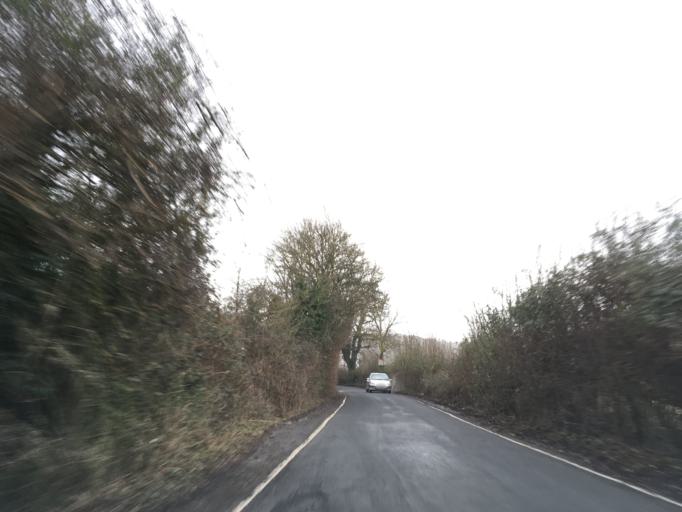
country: GB
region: England
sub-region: Gloucestershire
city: Cheltenham
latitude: 51.8732
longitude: -2.0923
